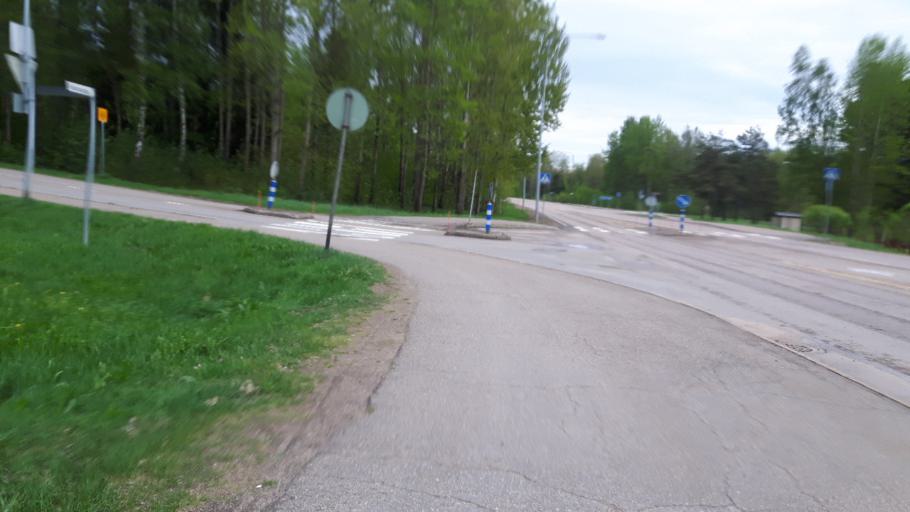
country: FI
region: Kymenlaakso
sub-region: Kotka-Hamina
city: Hamina
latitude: 60.5583
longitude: 27.2292
